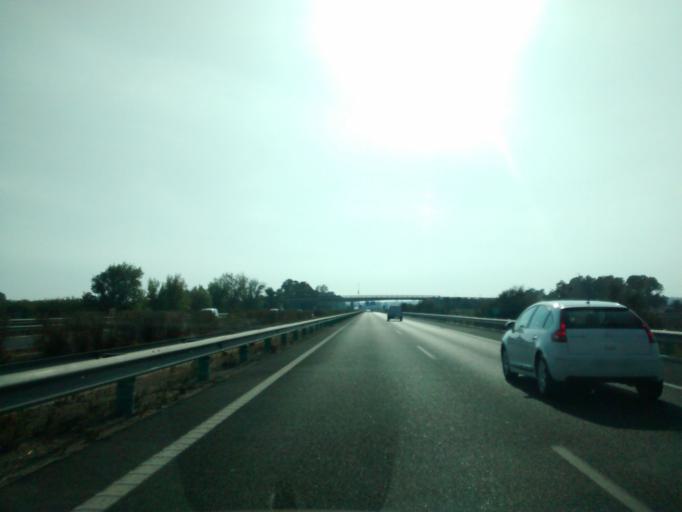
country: ES
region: Andalusia
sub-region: Provincia de Cadiz
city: Jerez de la Frontera
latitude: 36.7101
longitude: -6.0528
